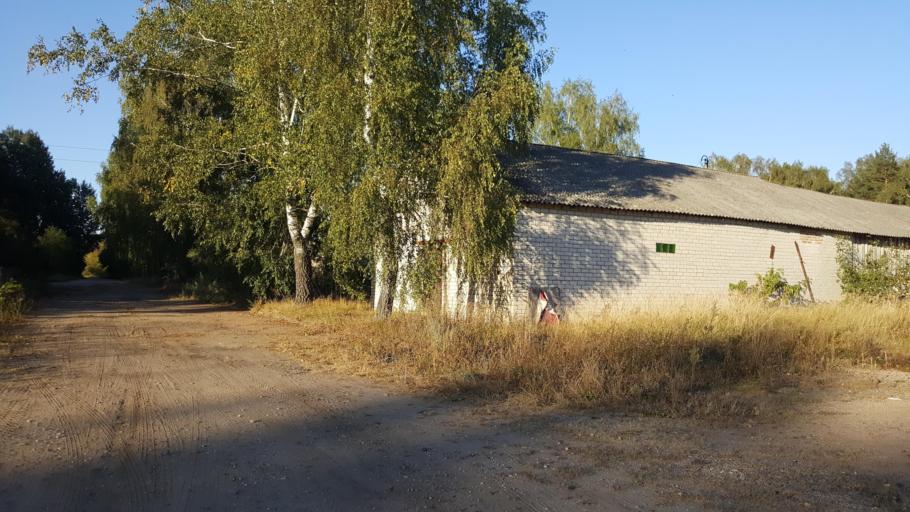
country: BY
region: Brest
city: Vysokaye
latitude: 52.3191
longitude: 23.4315
